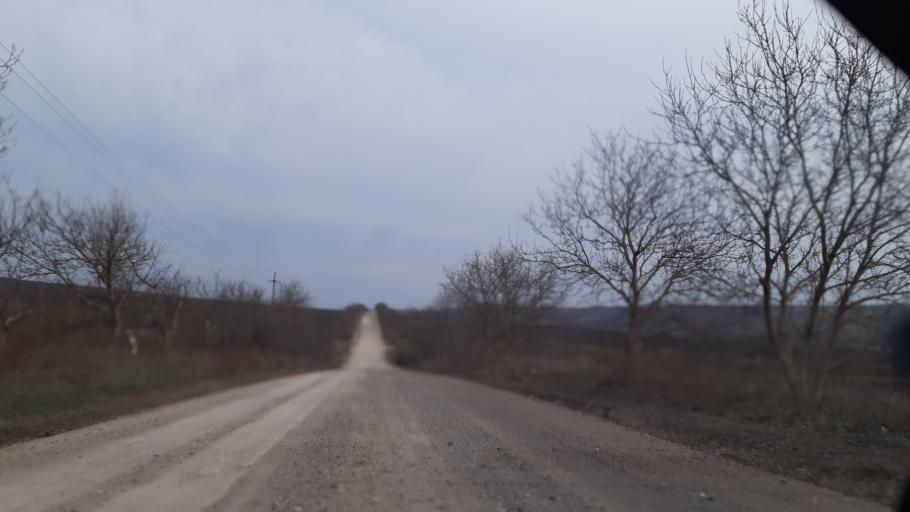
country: MD
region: Soldanesti
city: Soldanesti
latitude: 47.6983
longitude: 28.7270
